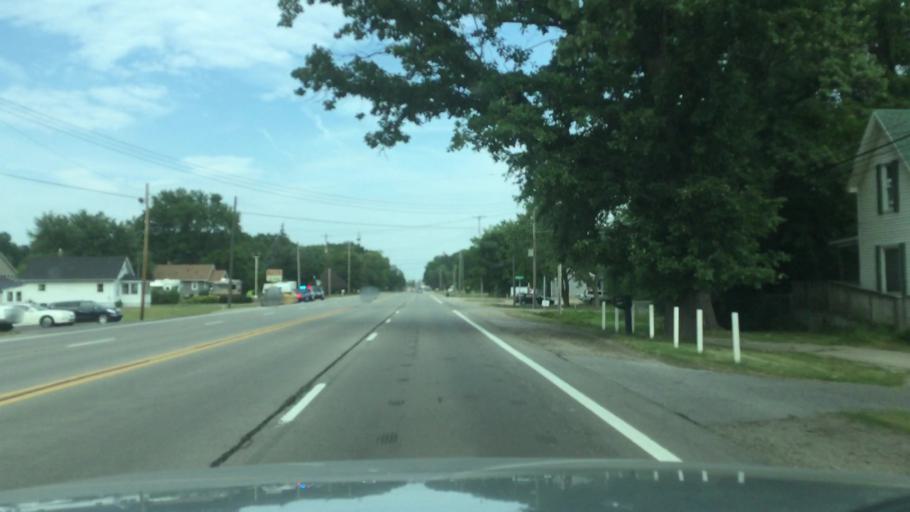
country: US
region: Michigan
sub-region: Genesee County
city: Swartz Creek
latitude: 43.0016
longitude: -83.7999
